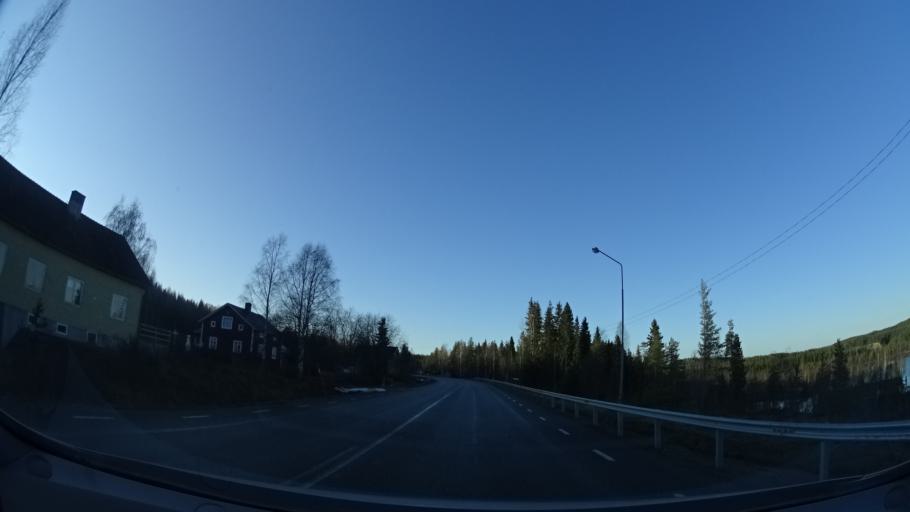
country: SE
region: Vaesterbotten
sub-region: Skelleftea Kommun
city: Langsele
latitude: 64.9245
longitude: 20.0420
